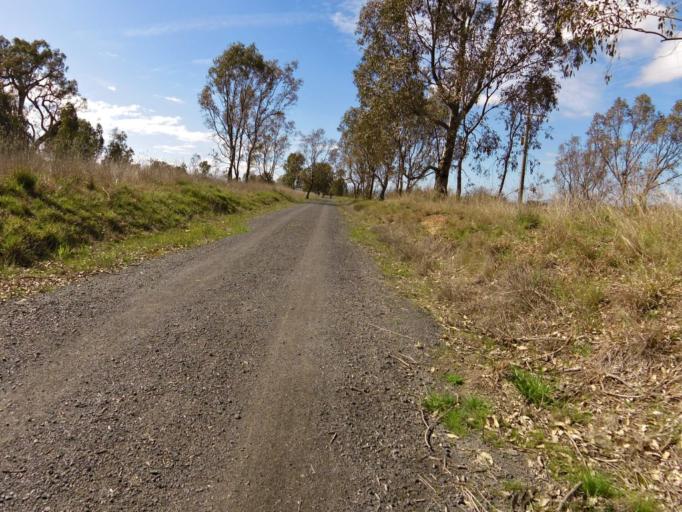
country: AU
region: Victoria
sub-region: Mansfield
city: Mansfield
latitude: -37.0489
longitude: 146.0669
